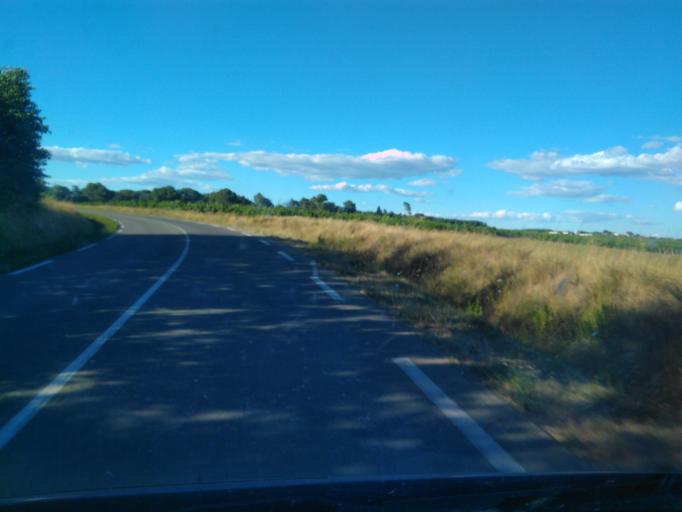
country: FR
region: Languedoc-Roussillon
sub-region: Departement du Gard
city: Vauvert
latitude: 43.6606
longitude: 4.2855
